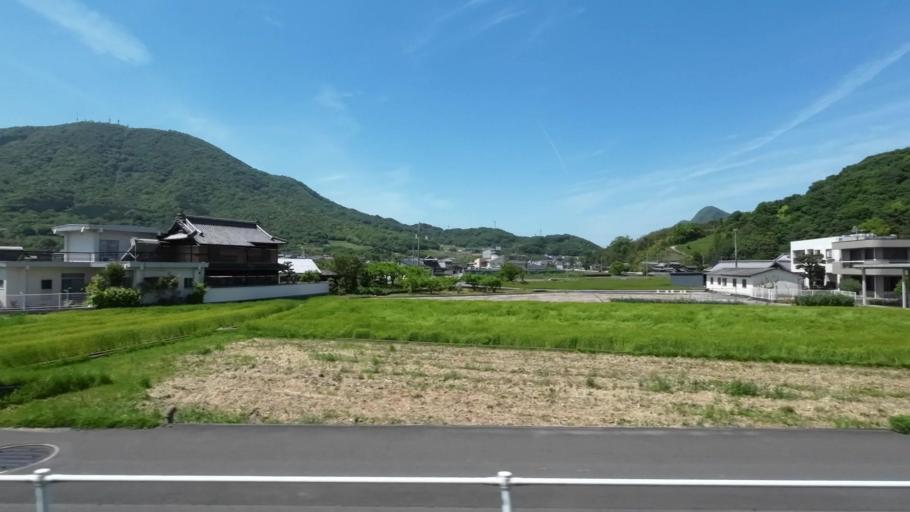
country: JP
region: Kagawa
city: Marugame
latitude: 34.2187
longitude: 133.7971
